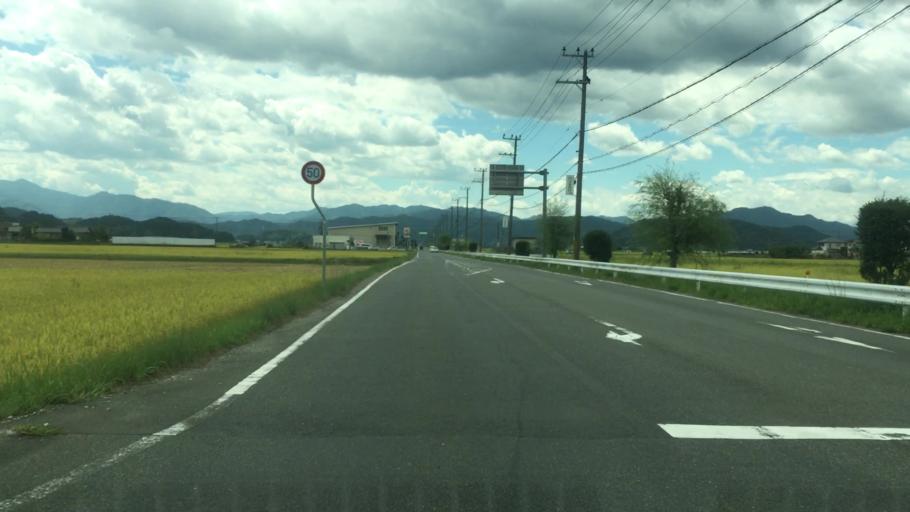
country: JP
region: Hyogo
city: Toyooka
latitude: 35.5276
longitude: 134.8398
